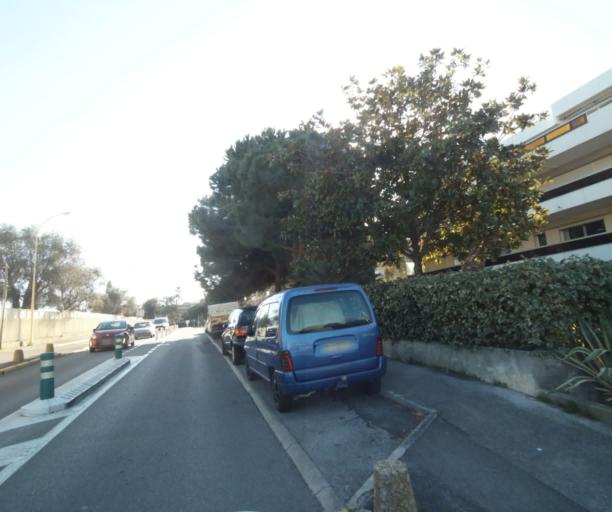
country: FR
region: Provence-Alpes-Cote d'Azur
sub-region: Departement des Alpes-Maritimes
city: Biot
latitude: 43.6030
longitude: 7.1215
